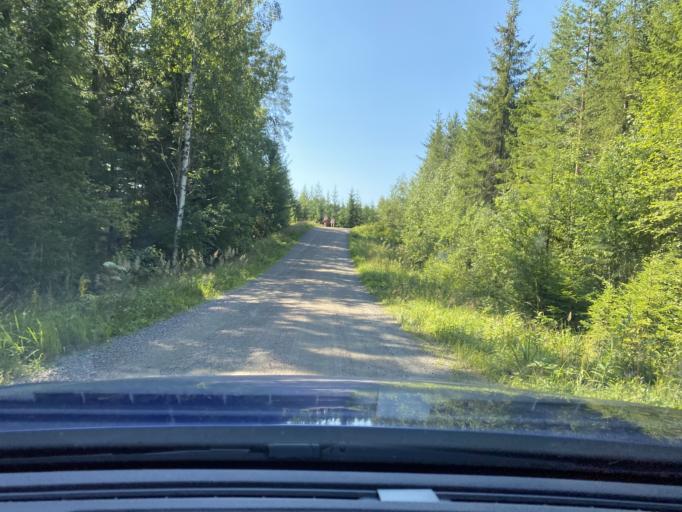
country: FI
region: Central Finland
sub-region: Jaemsae
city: Jaemsae
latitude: 61.8524
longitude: 25.3855
